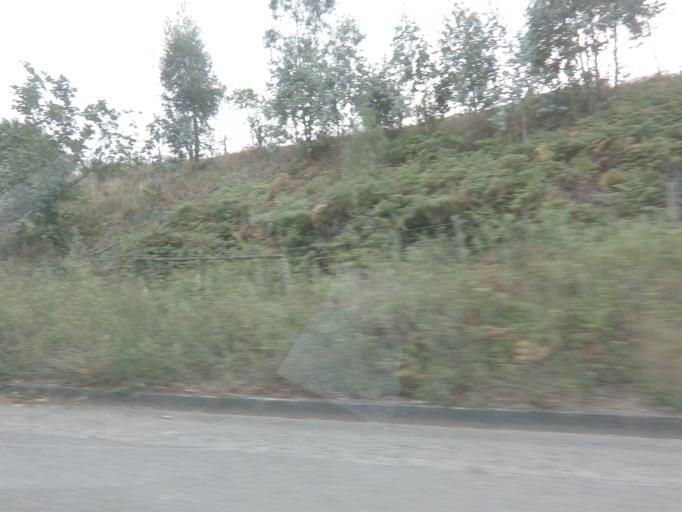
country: PT
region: Aveiro
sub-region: Mealhada
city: Pampilhosa do Botao
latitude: 40.3050
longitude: -8.3671
